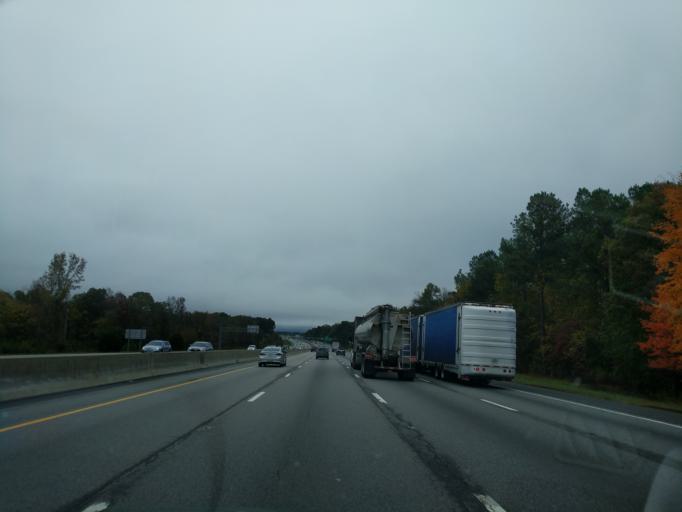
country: US
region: North Carolina
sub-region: Alamance County
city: Mebane
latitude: 36.0748
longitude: -79.1892
